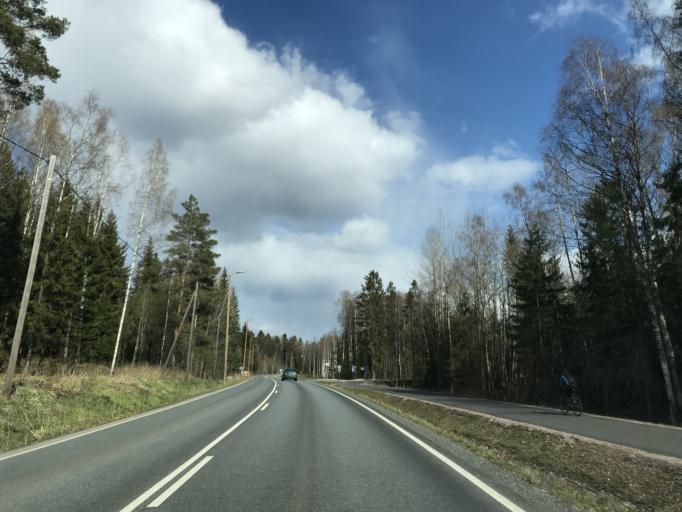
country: FI
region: Uusimaa
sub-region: Helsinki
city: Jaervenpaeae
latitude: 60.4819
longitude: 25.0465
